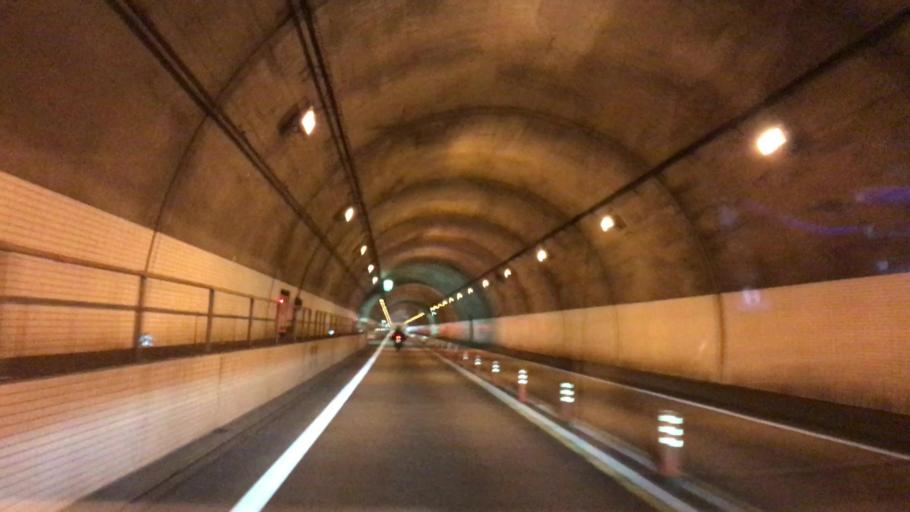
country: JP
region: Hokkaido
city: Chitose
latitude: 42.9172
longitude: 141.9482
